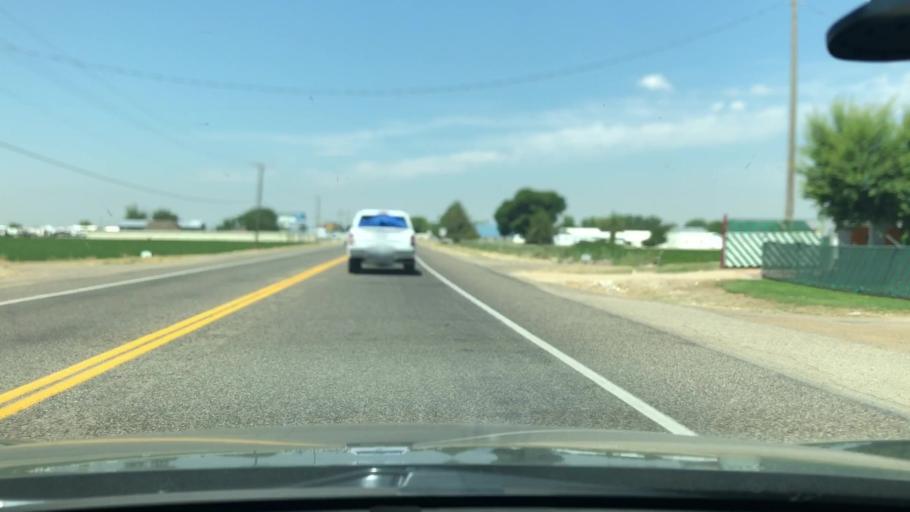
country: US
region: Idaho
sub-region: Canyon County
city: Wilder
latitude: 43.6641
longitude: -116.9120
